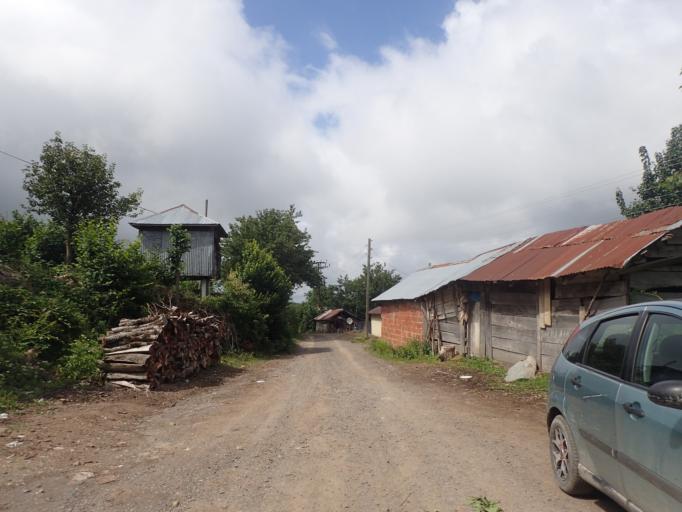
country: TR
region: Ordu
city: Akkus
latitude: 40.8587
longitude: 37.0089
